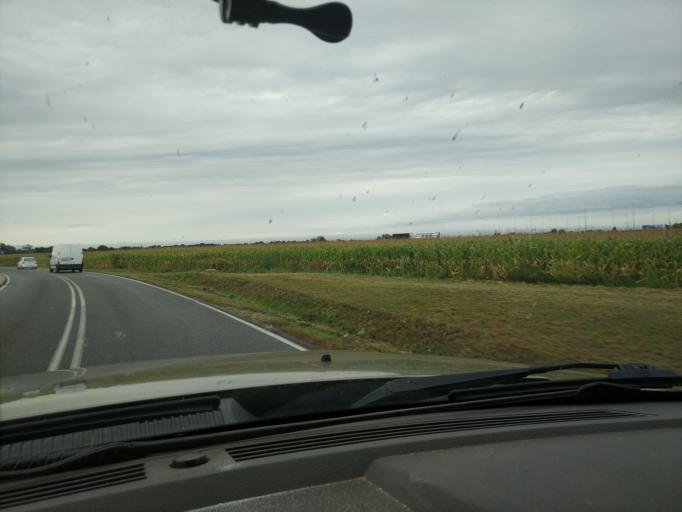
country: PL
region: Masovian Voivodeship
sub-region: Powiat pruszkowski
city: Brwinow
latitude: 52.1635
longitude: 20.7370
